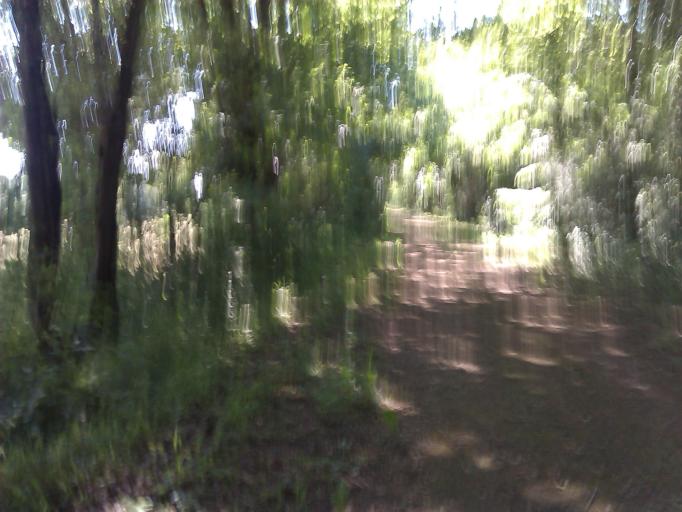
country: FR
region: Centre
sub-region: Departement de l'Indre
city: Saint-Gaultier
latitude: 46.6438
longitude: 1.3209
